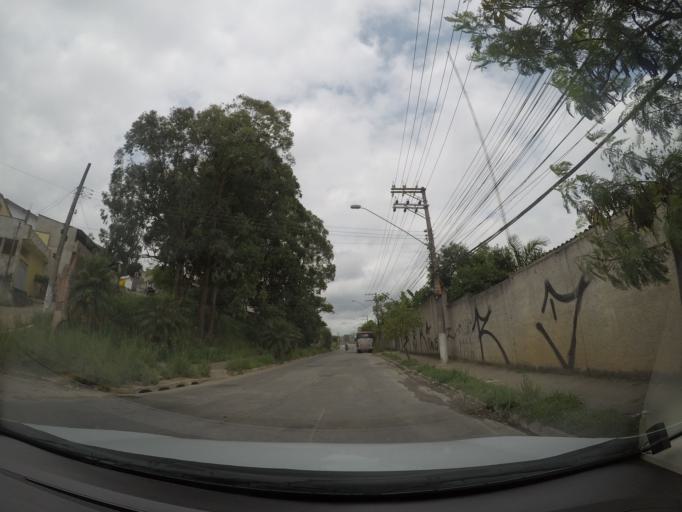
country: BR
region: Sao Paulo
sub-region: Itaquaquecetuba
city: Itaquaquecetuba
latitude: -23.4424
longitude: -46.3911
